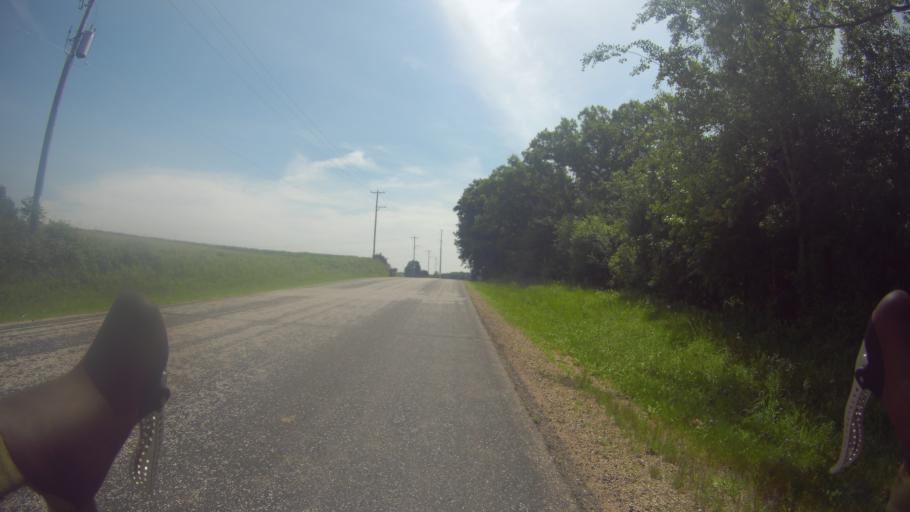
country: US
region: Wisconsin
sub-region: Dane County
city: Deerfield
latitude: 43.0453
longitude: -89.0458
